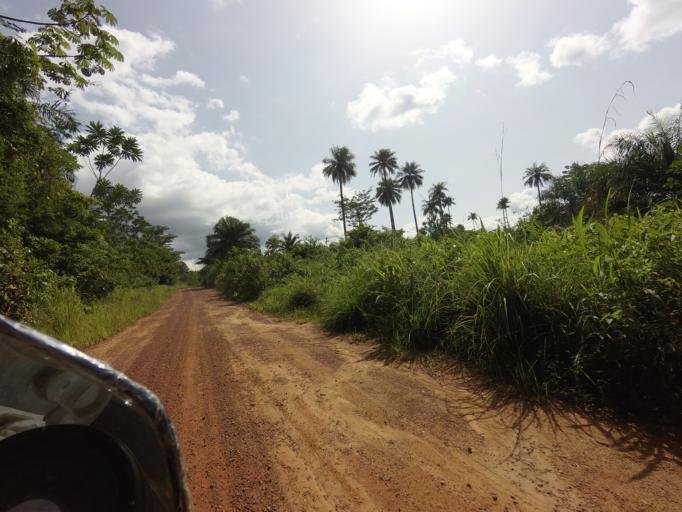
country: SL
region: Eastern Province
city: Daru
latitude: 8.0359
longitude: -10.8768
